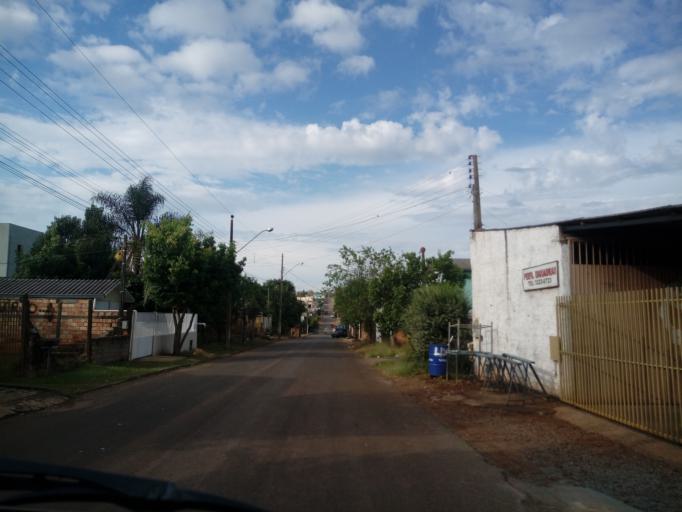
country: BR
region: Santa Catarina
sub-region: Chapeco
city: Chapeco
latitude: -27.0927
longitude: -52.5919
